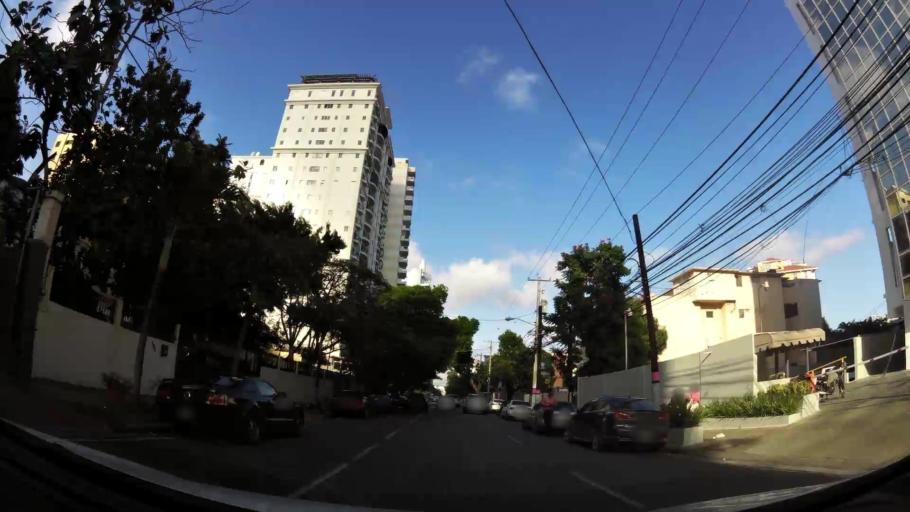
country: DO
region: Nacional
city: La Julia
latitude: 18.4662
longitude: -69.9234
